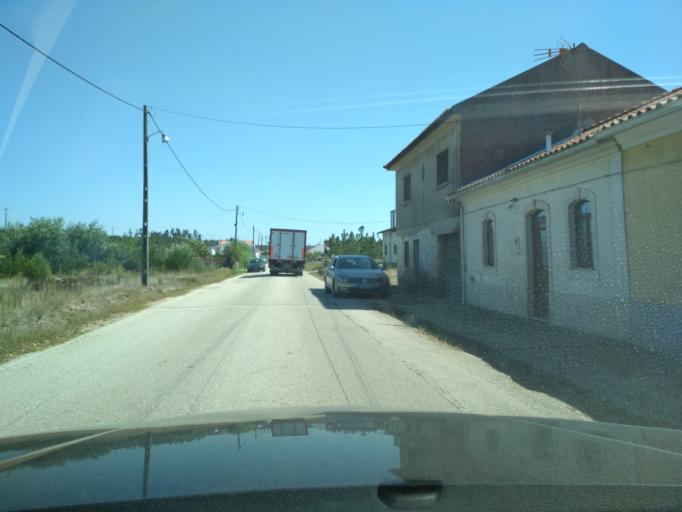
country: PT
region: Coimbra
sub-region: Figueira da Foz
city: Lavos
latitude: 40.0534
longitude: -8.8683
